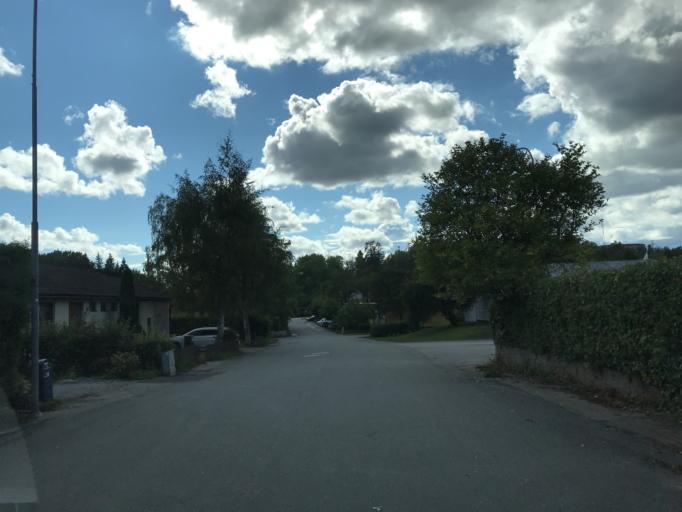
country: SE
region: Stockholm
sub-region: Sollentuna Kommun
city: Sollentuna
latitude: 59.4515
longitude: 17.9605
